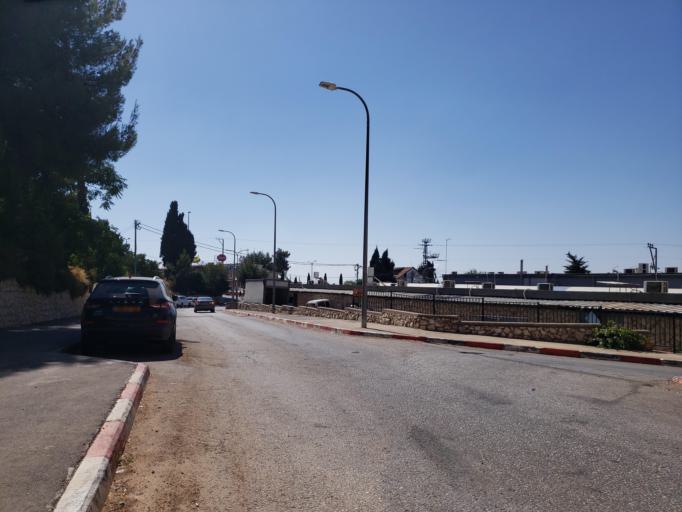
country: IL
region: Northern District
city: Safed
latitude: 32.9580
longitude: 35.4963
